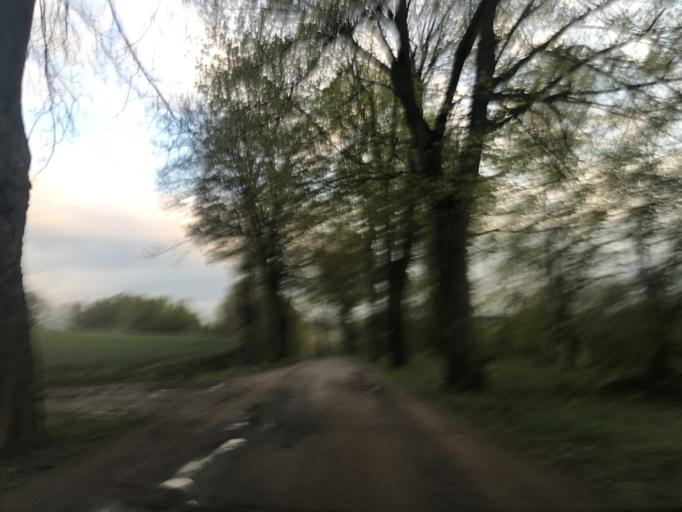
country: PL
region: Warmian-Masurian Voivodeship
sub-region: Powiat ilawski
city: Lubawa
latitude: 53.5408
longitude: 19.8969
